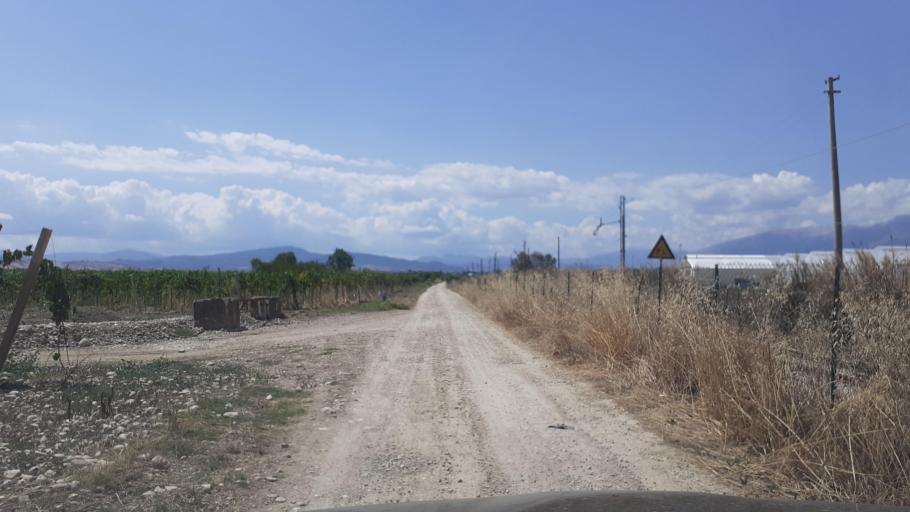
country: IT
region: Abruzzo
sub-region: Provincia di Chieti
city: Fossacesia
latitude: 42.2057
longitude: 14.4921
